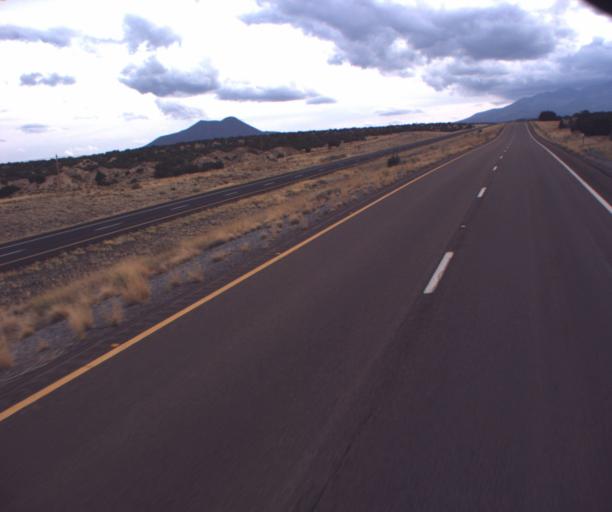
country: US
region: Arizona
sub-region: Coconino County
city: Flagstaff
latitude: 35.5111
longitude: -111.5466
